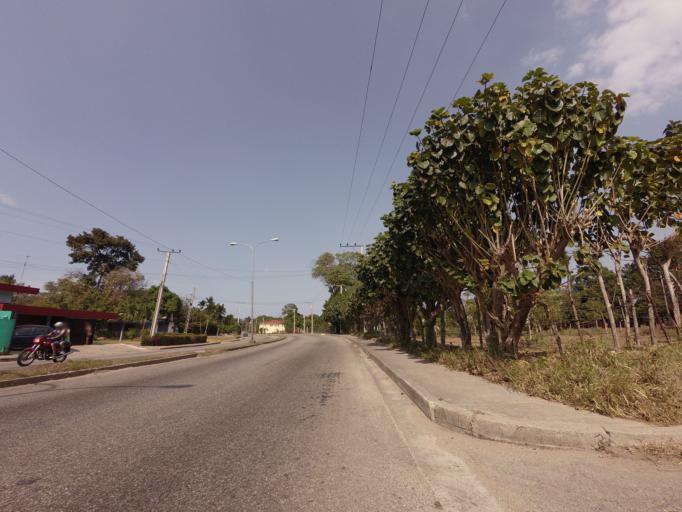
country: CU
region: La Habana
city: Cerro
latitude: 23.0780
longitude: -82.4501
